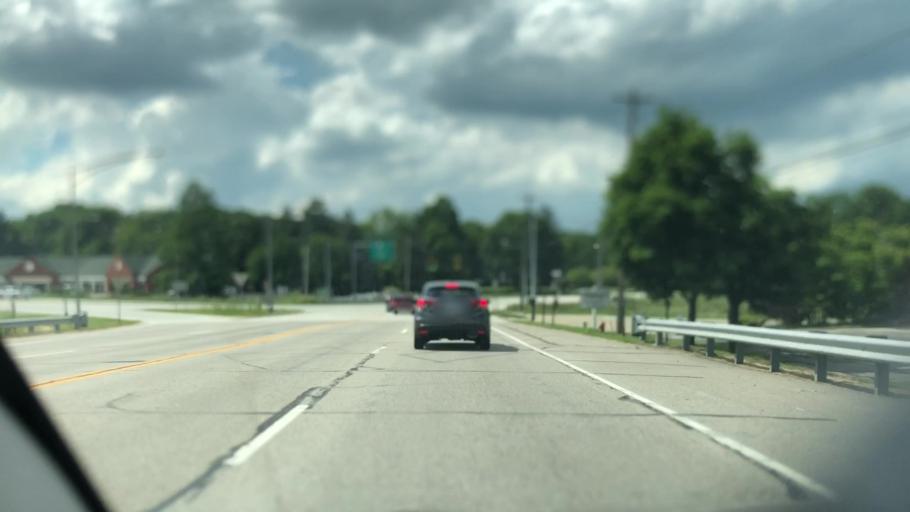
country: US
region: Ohio
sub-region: Summit County
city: Montrose-Ghent
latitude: 41.1513
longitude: -81.6317
